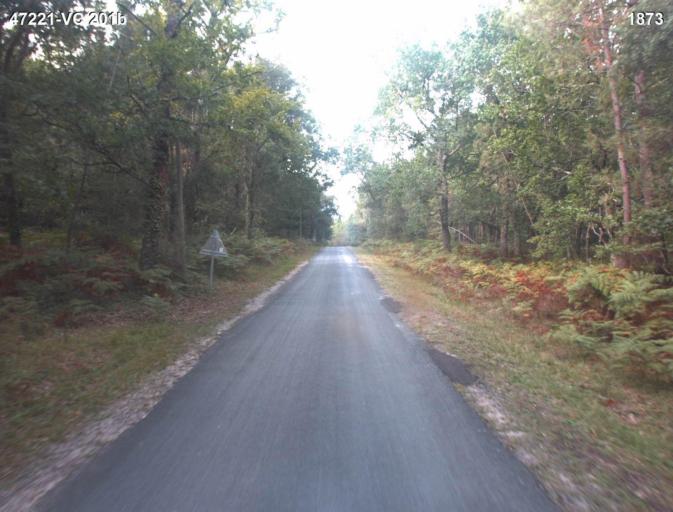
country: FR
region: Aquitaine
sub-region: Departement du Lot-et-Garonne
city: Mezin
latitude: 44.0811
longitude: 0.2283
